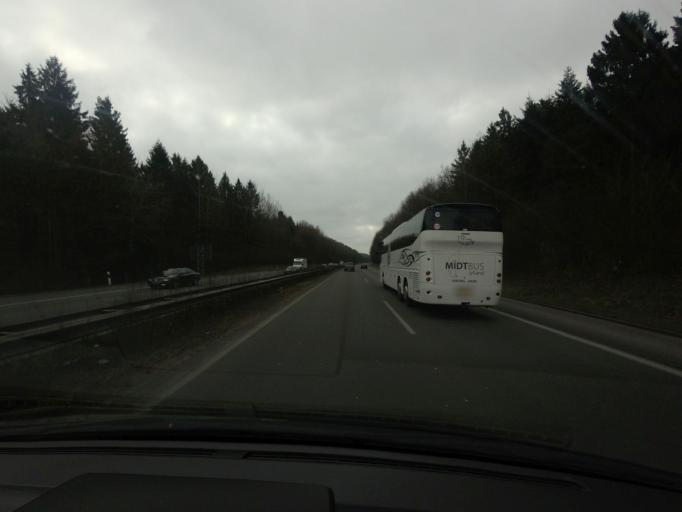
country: DE
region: Lower Saxony
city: Seevetal
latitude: 53.4183
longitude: 9.9250
